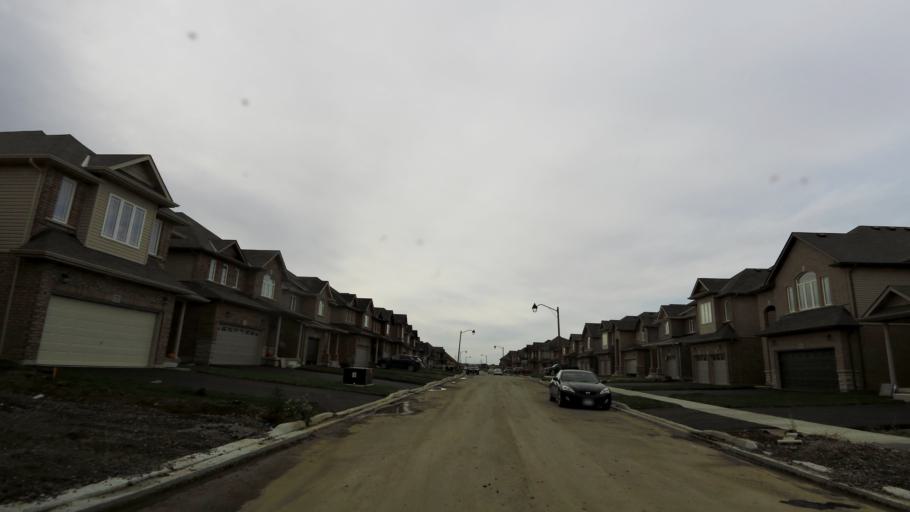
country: CA
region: Ontario
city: Hamilton
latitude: 43.1755
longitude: -79.7987
